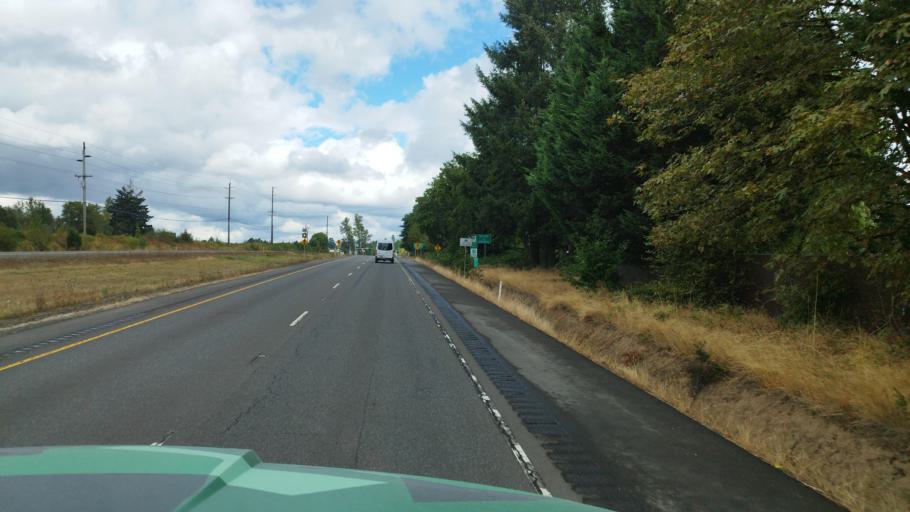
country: US
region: Oregon
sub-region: Washington County
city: Sherwood
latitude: 45.3496
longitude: -122.8697
